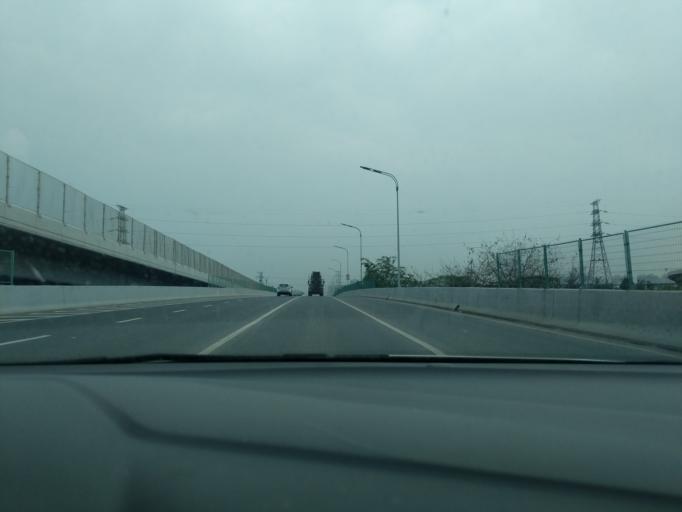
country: CN
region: Guangdong
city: Huangge
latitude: 22.8549
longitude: 113.4901
